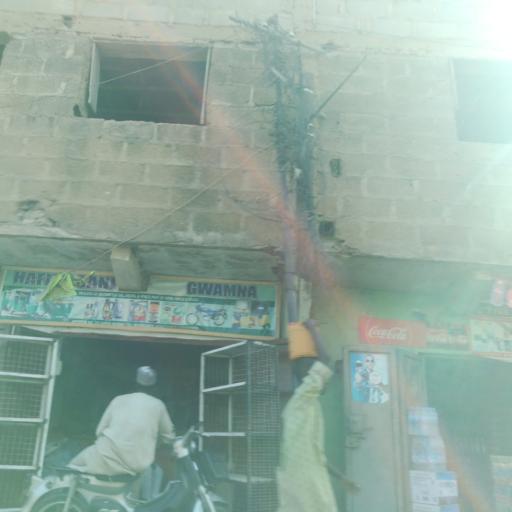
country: NG
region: Kano
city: Kano
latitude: 12.0056
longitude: 8.5211
